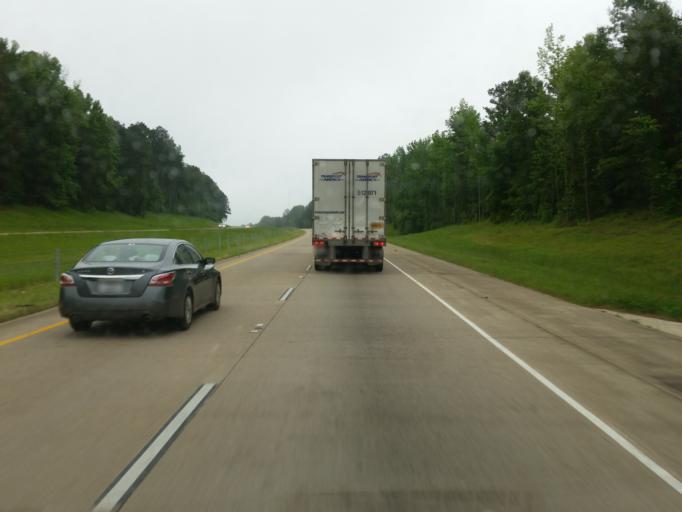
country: US
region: Louisiana
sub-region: Bienville Parish
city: Arcadia
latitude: 32.5609
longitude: -93.0273
